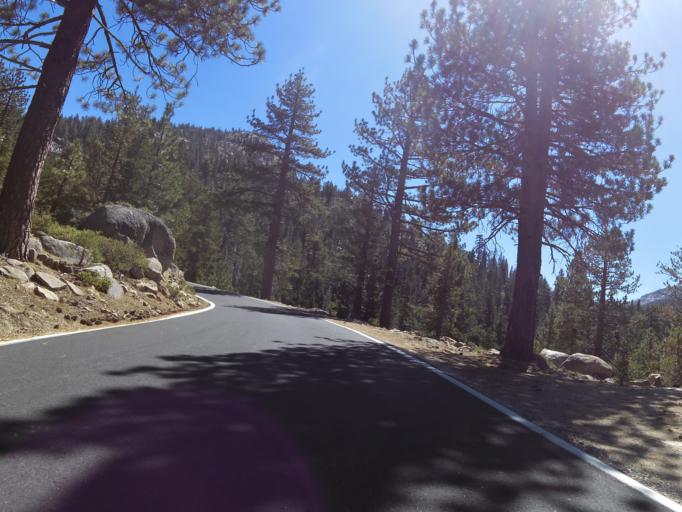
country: US
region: Nevada
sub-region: Douglas County
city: Gardnerville Ranchos
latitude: 38.5422
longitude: -119.8768
